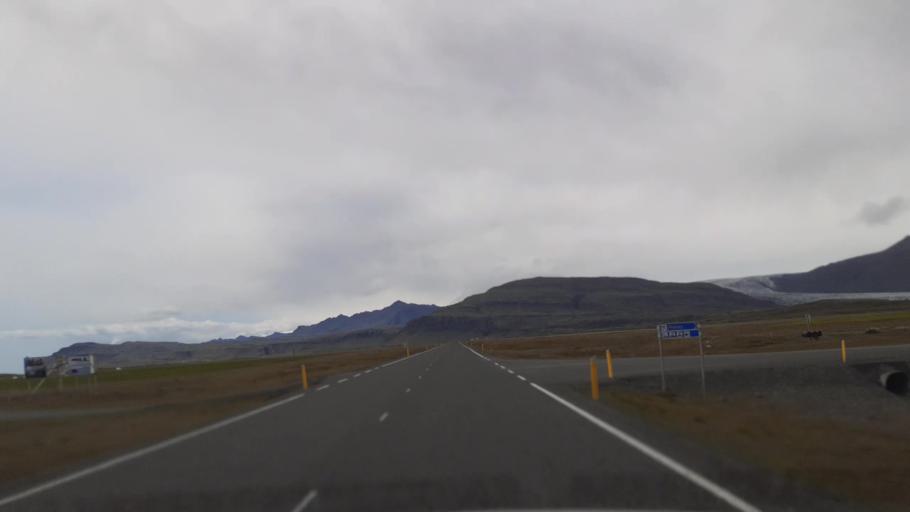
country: IS
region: East
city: Hoefn
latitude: 64.2575
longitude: -15.5828
